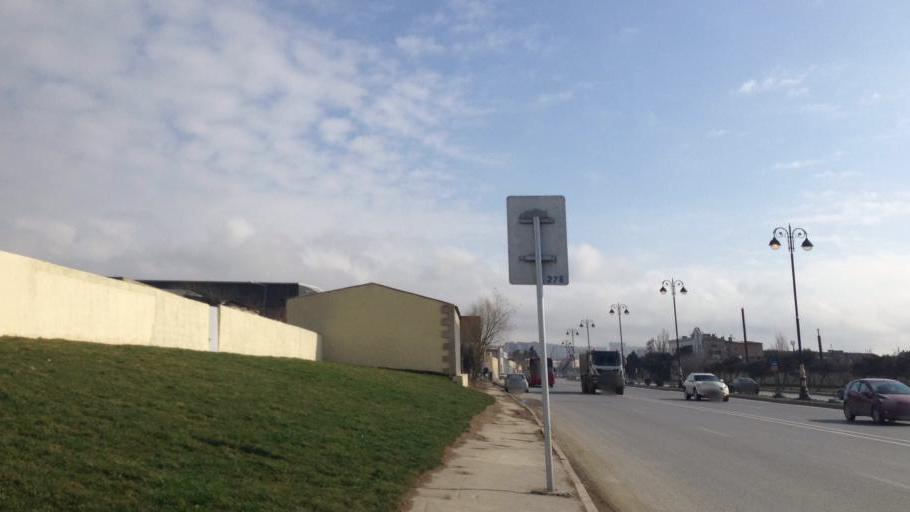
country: AZ
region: Baki
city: Baku
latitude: 40.3764
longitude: 49.9149
